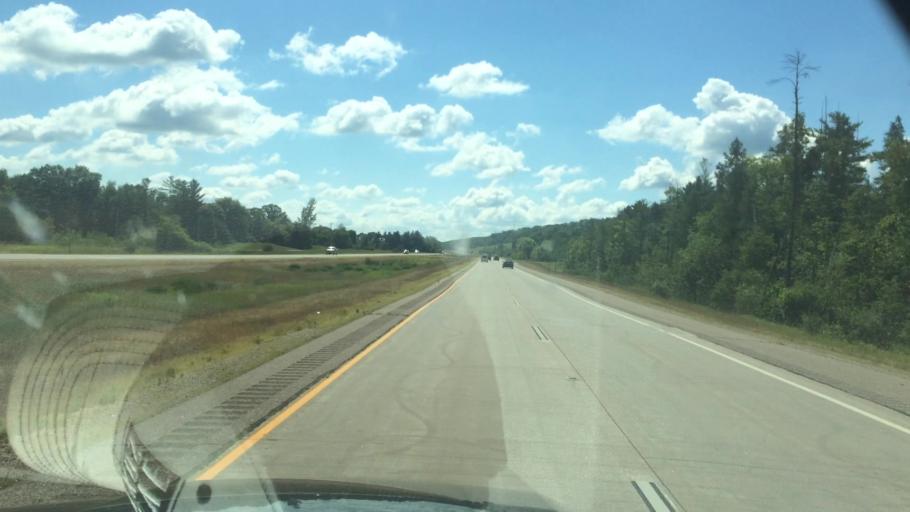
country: US
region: Wisconsin
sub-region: Waupaca County
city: King
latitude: 44.3825
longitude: -89.1776
